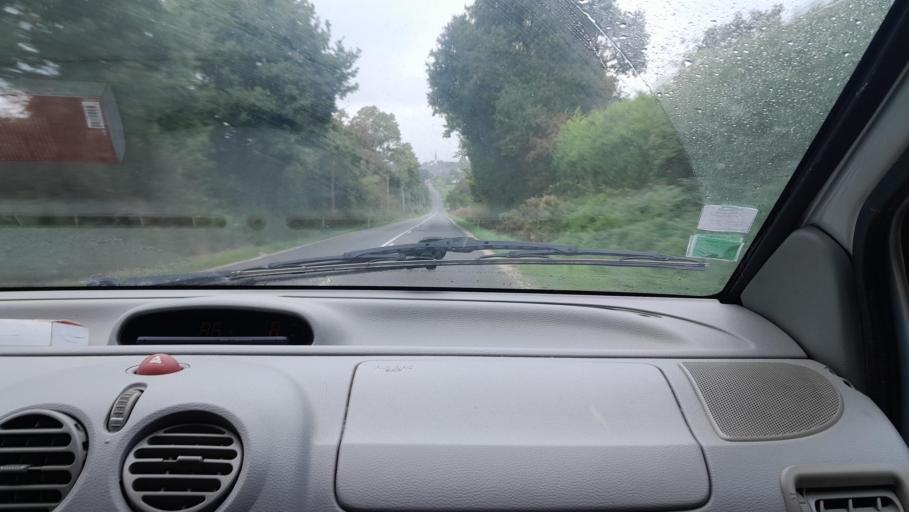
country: FR
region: Pays de la Loire
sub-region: Departement de la Mayenne
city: Congrier
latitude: 47.8306
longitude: -1.1414
